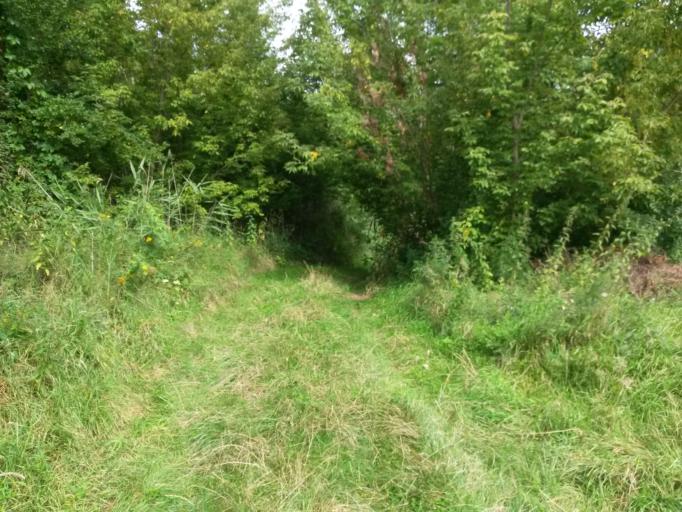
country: DE
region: Brandenburg
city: Oderberg
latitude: 52.8638
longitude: 14.0621
